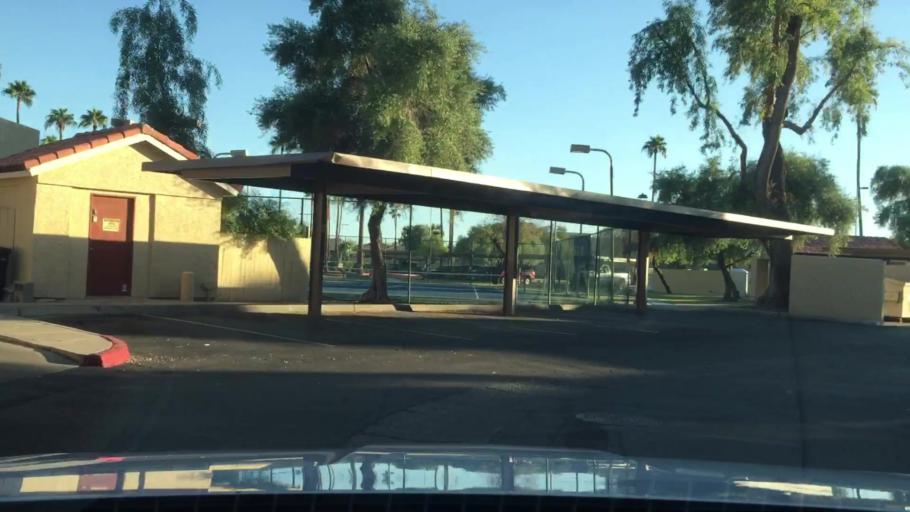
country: US
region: Arizona
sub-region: Maricopa County
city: Chandler
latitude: 33.3270
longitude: -111.8267
